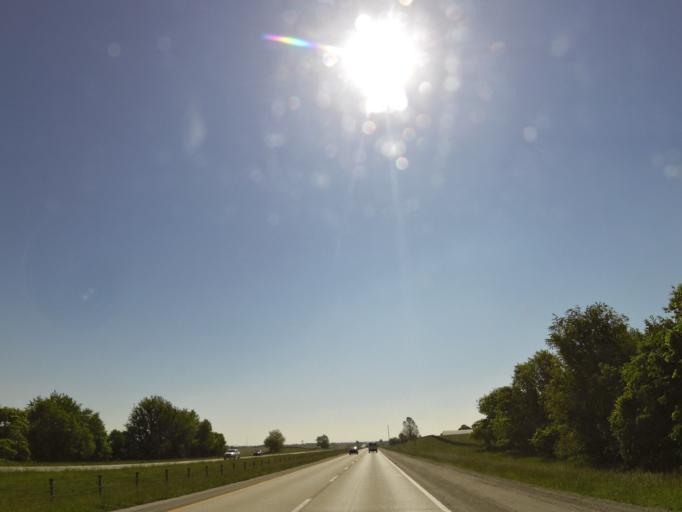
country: US
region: Kentucky
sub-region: Woodford County
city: Midway
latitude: 38.1620
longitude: -84.7210
